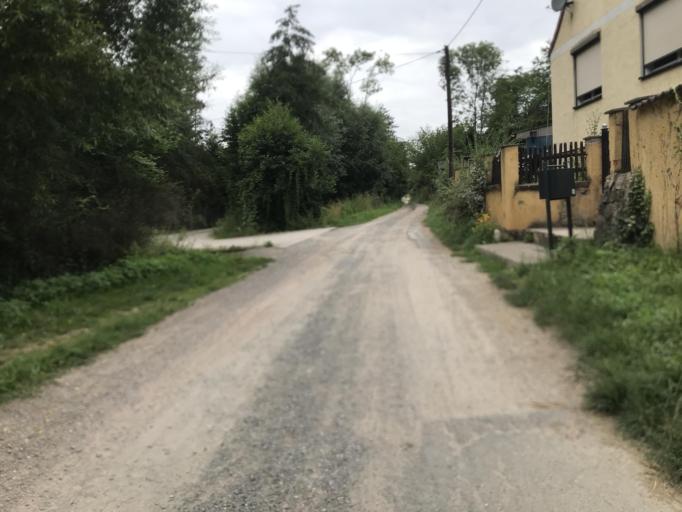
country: DE
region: Saxony-Anhalt
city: Thale
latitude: 51.7569
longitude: 11.0243
